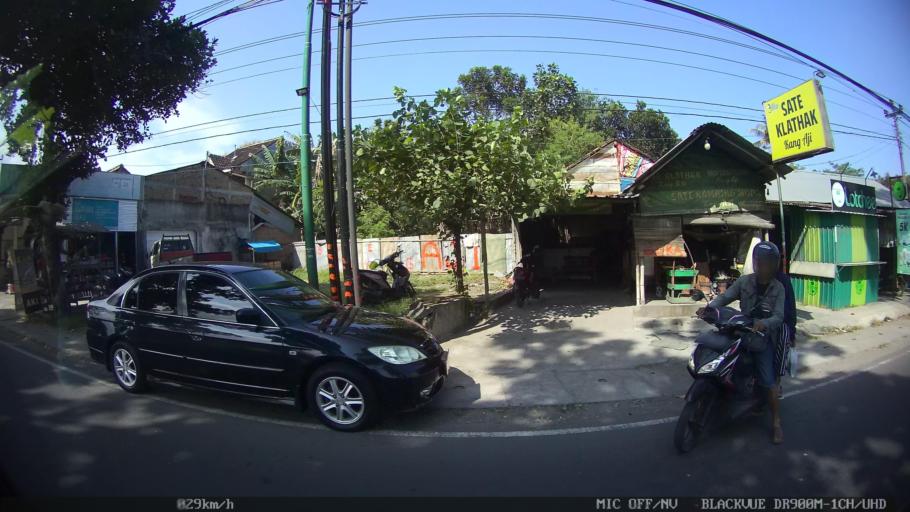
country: ID
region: Daerah Istimewa Yogyakarta
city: Sewon
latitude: -7.8673
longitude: 110.3903
